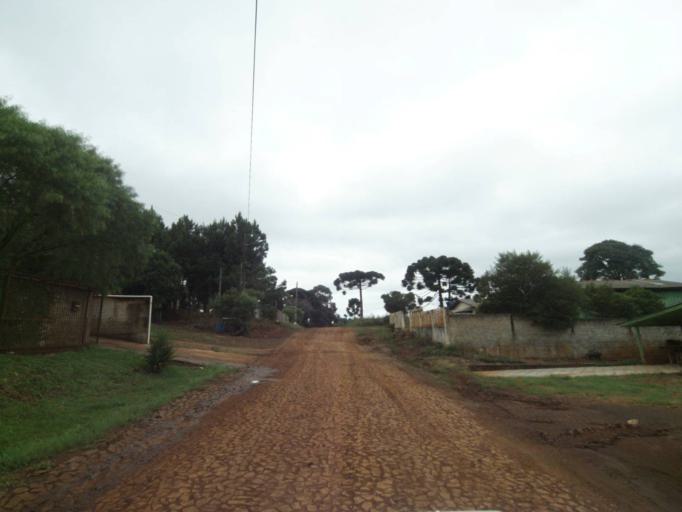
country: BR
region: Parana
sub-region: Pitanga
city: Pitanga
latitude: -24.9349
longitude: -51.8674
